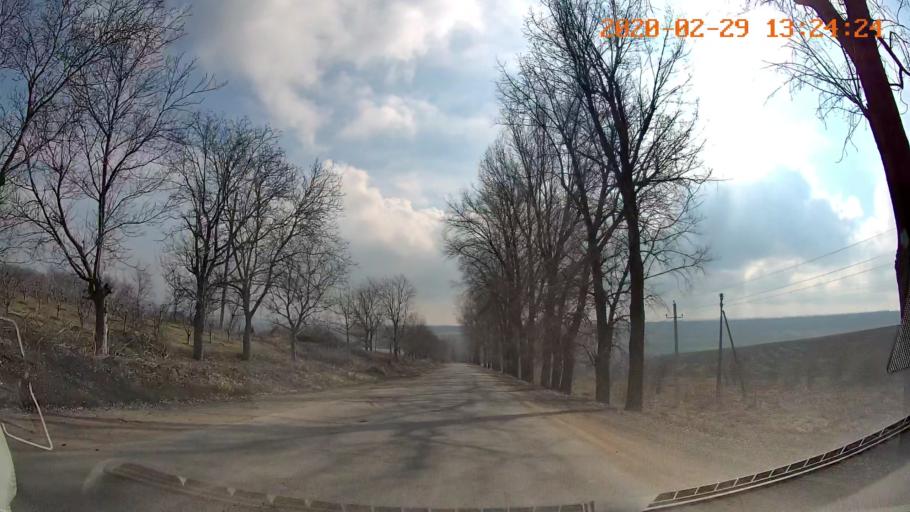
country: MD
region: Telenesti
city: Camenca
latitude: 47.9392
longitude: 28.6273
